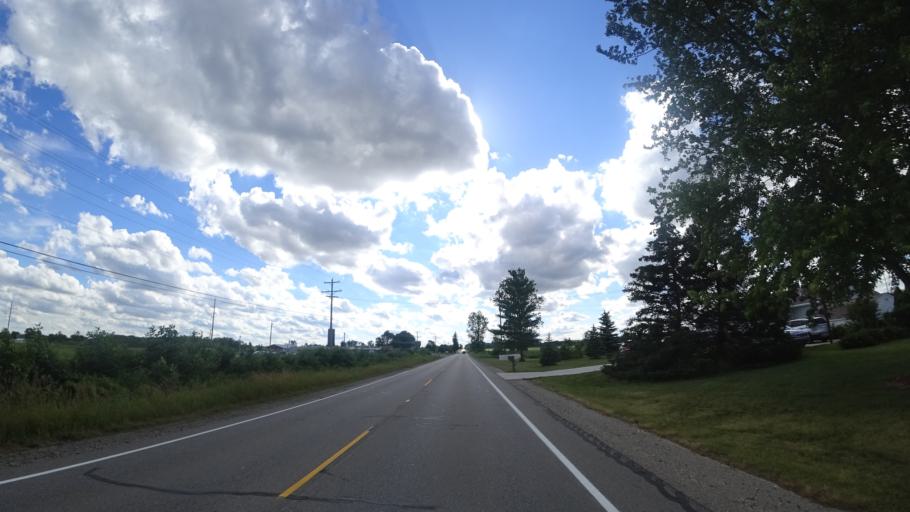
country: US
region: Michigan
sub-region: Ionia County
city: Portland
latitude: 42.8716
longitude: -84.9241
